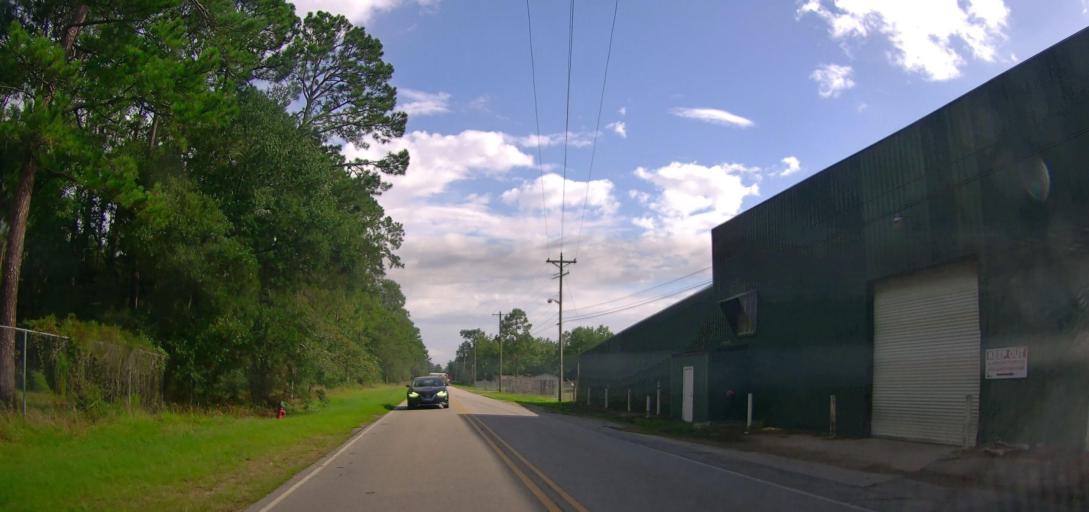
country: US
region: Georgia
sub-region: Coffee County
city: Douglas
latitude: 31.4924
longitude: -82.8590
